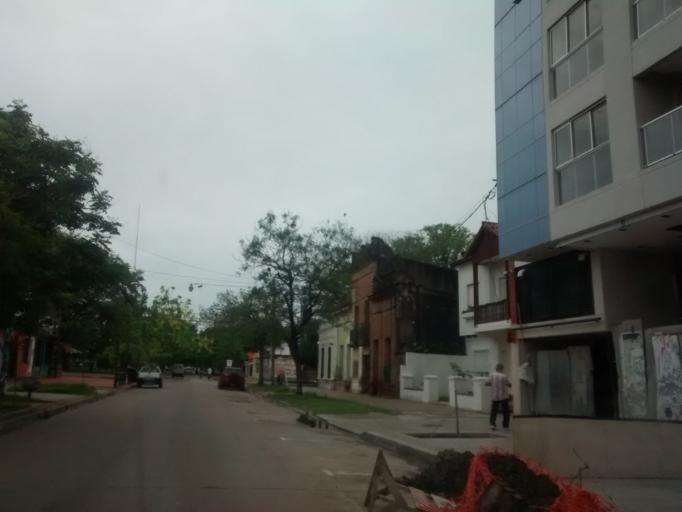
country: AR
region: Chaco
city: Resistencia
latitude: -27.4499
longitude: -58.9809
